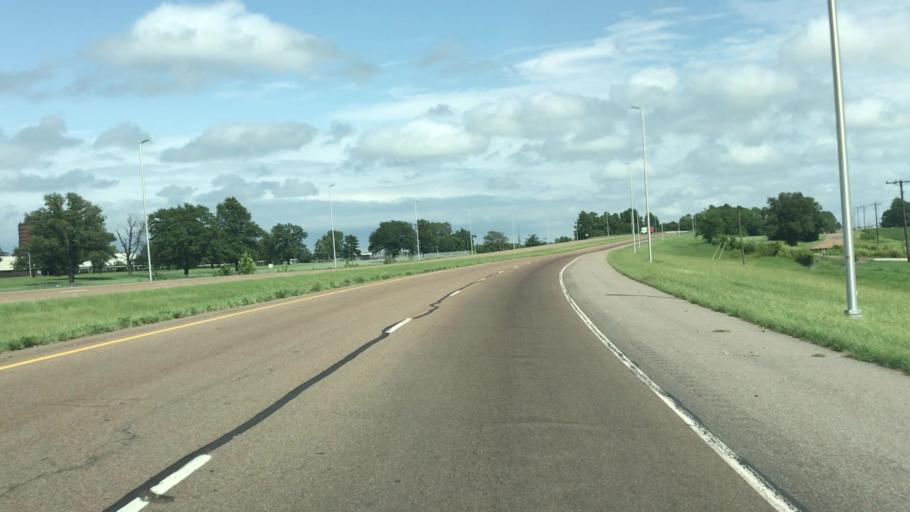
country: US
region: Tennessee
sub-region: Obion County
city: Union City
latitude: 36.4481
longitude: -89.0621
